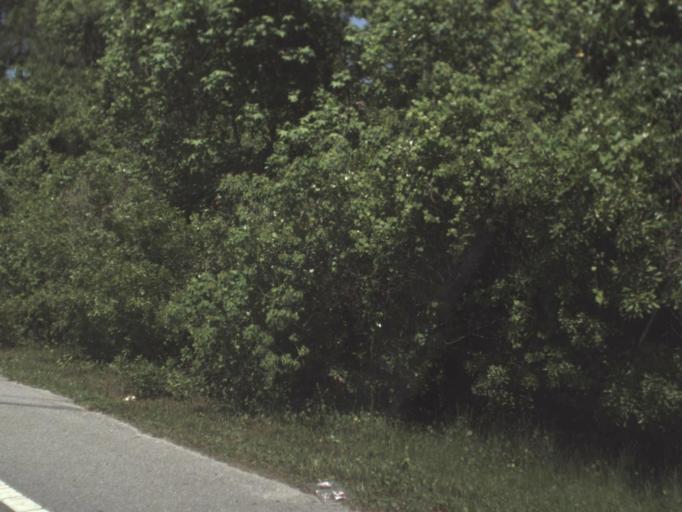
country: US
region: Florida
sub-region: Bay County
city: Pretty Bayou
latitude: 30.1795
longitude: -85.6837
